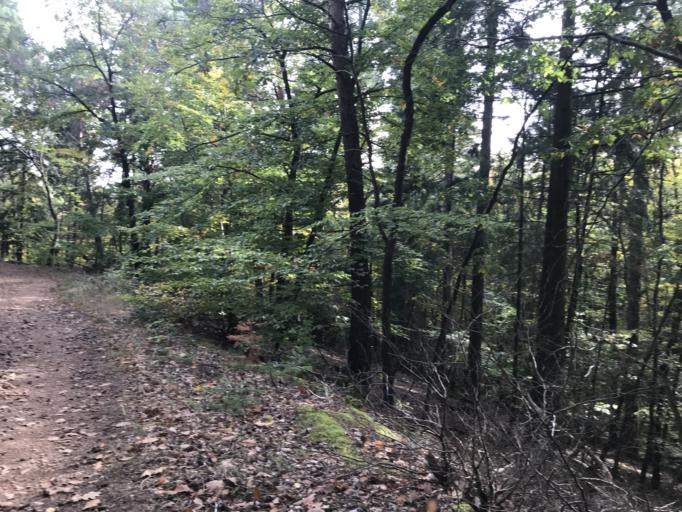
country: DE
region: Rheinland-Pfalz
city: Kirchheimbolanden
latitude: 49.6557
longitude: 7.9918
